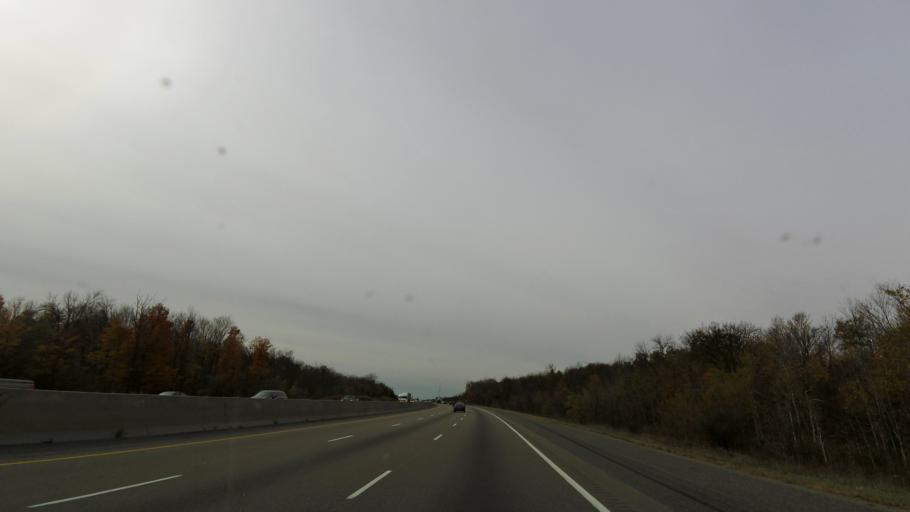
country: CA
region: Ontario
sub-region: Halton
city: Milton
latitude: 43.4718
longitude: -80.0617
